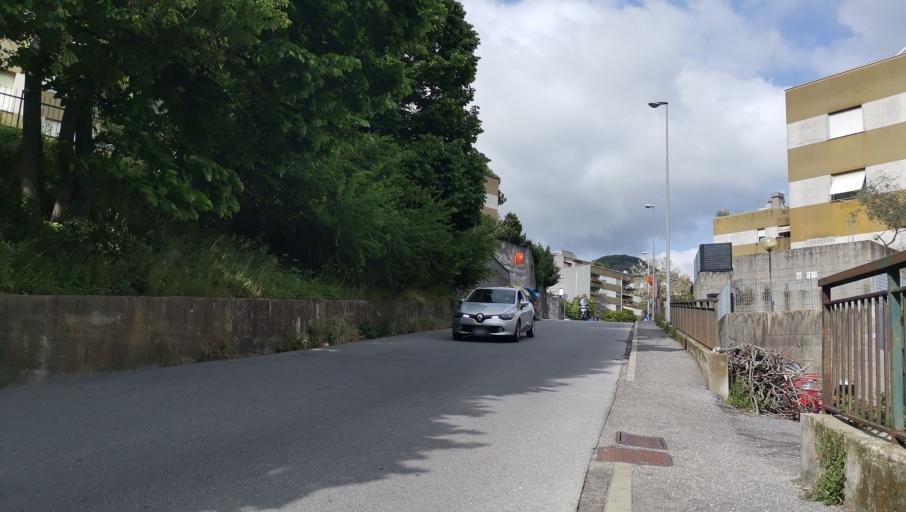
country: IT
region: Liguria
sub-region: Provincia di Genova
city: Piccarello
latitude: 44.4495
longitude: 9.0017
